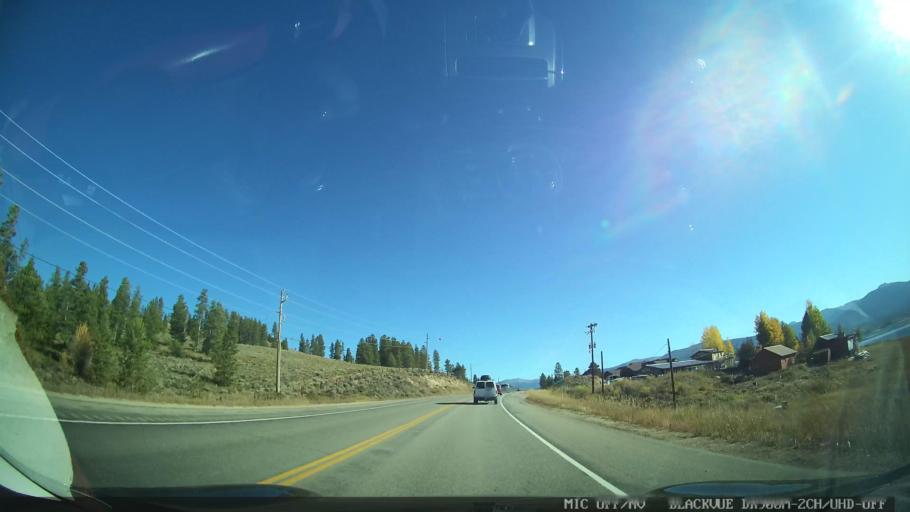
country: US
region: Colorado
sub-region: Grand County
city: Granby
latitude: 40.1748
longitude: -105.9000
